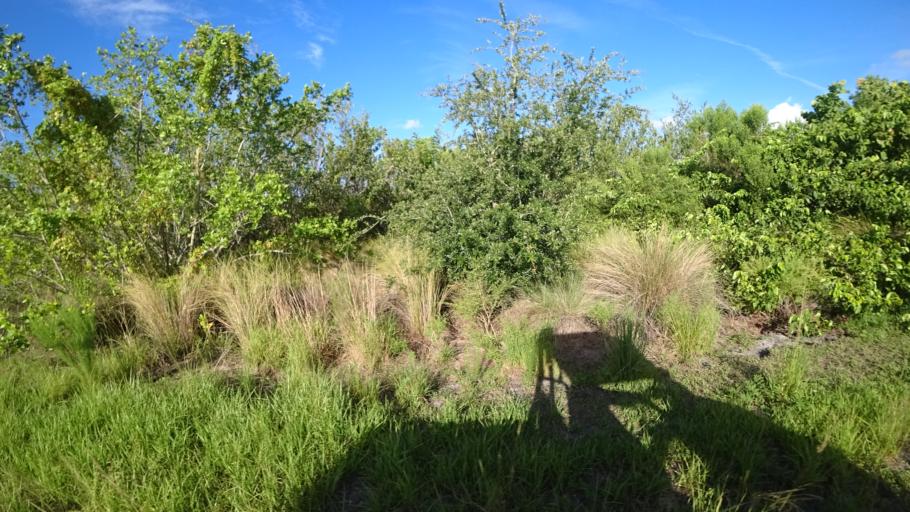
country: US
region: Florida
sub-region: Manatee County
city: Cortez
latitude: 27.5045
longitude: -82.6673
